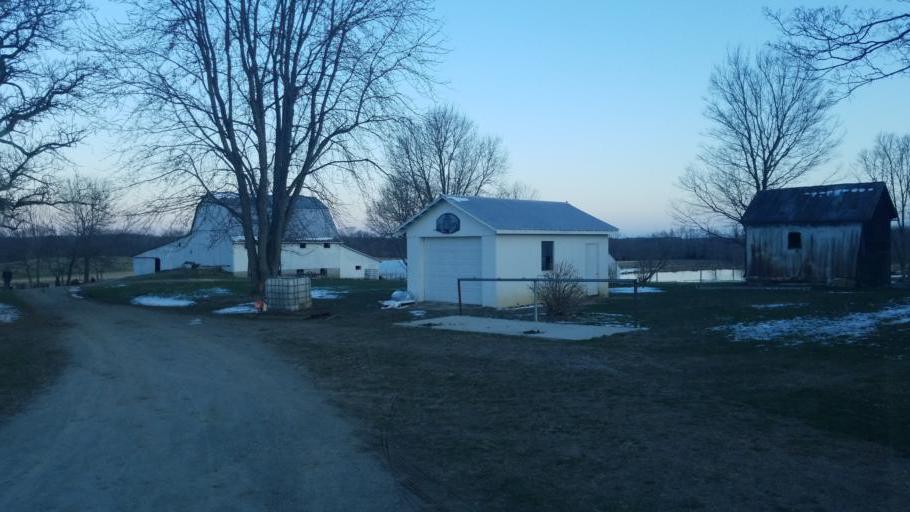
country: US
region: Ohio
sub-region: Highland County
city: Leesburg
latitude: 39.2867
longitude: -83.5185
